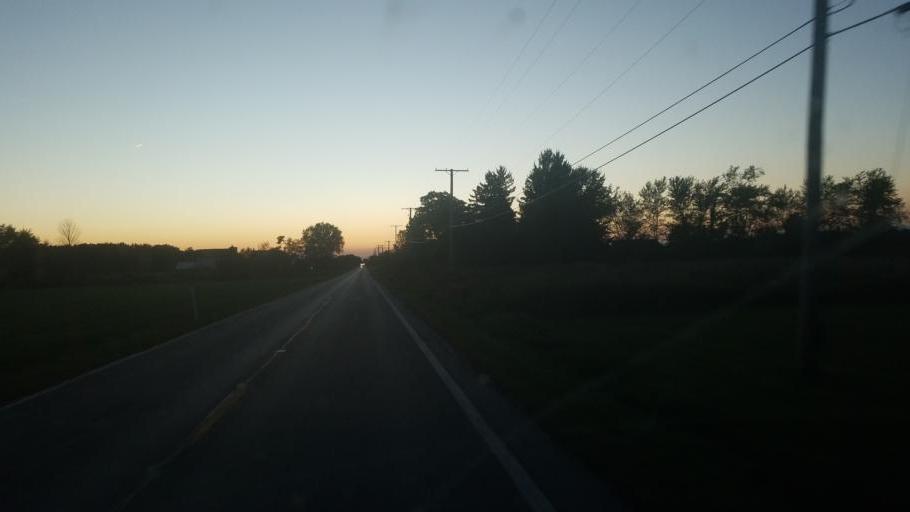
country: US
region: Ohio
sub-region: Ashtabula County
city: Jefferson
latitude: 41.7519
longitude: -80.6511
